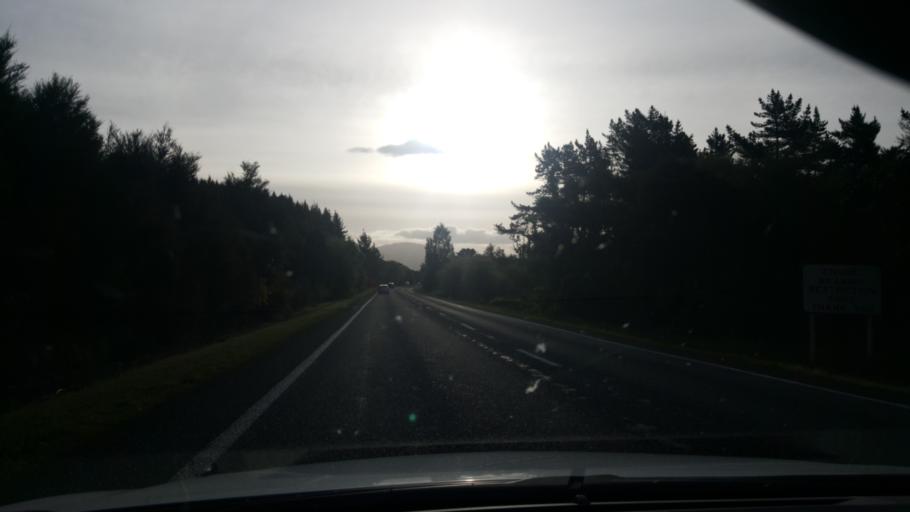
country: NZ
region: Waikato
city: Turangi
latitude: -38.9368
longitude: 175.8661
